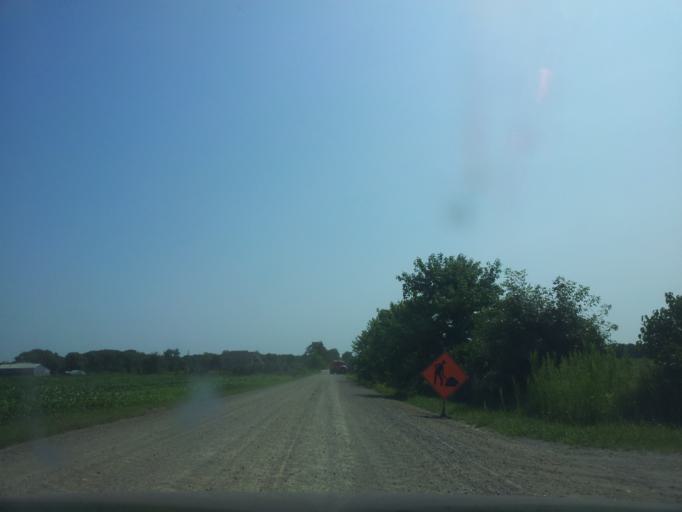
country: CA
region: Ontario
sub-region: Oxford County
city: Woodstock
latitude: 42.9515
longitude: -80.6371
